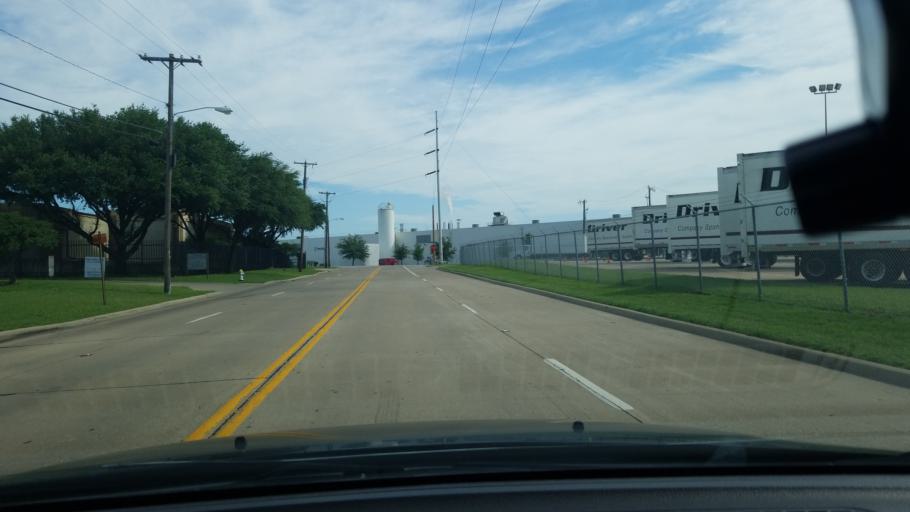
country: US
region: Texas
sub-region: Dallas County
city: Balch Springs
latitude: 32.7730
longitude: -96.6567
